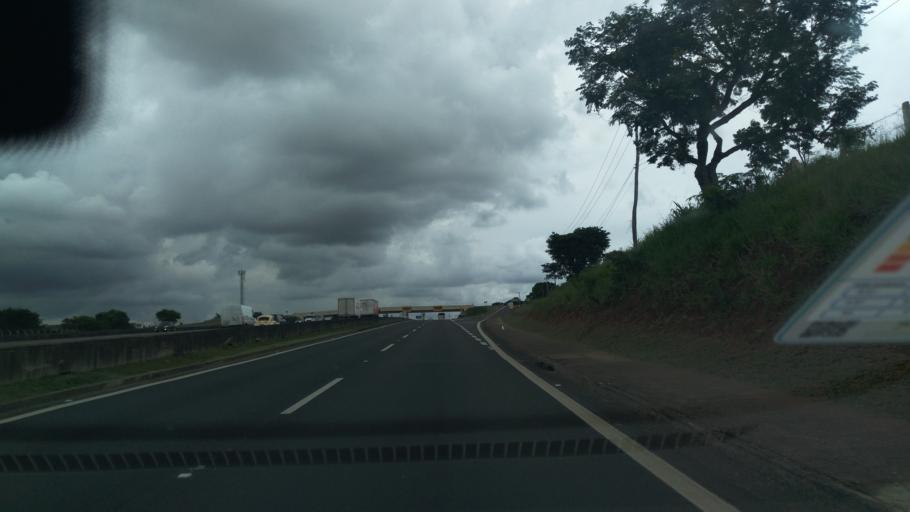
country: BR
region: Sao Paulo
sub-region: Campinas
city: Campinas
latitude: -22.8747
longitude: -47.1235
